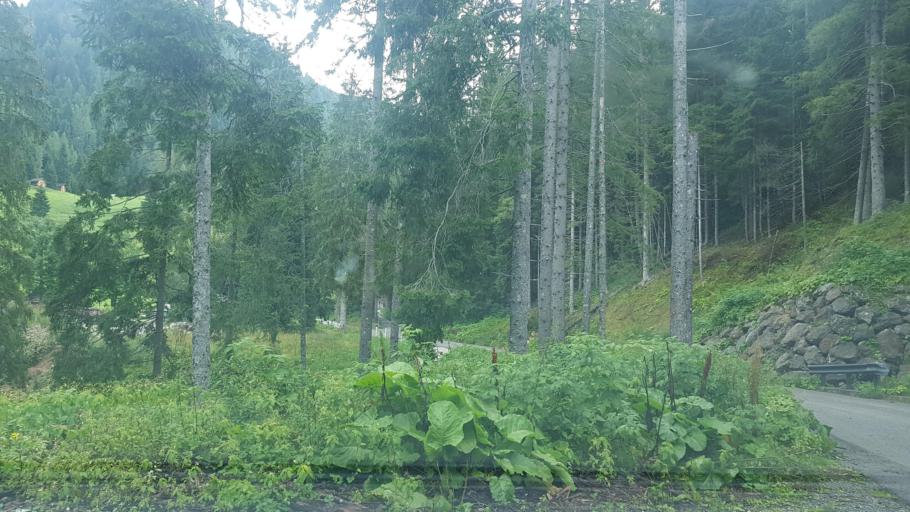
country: IT
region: Veneto
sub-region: Provincia di Belluno
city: Granvilla
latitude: 46.5729
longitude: 12.7277
